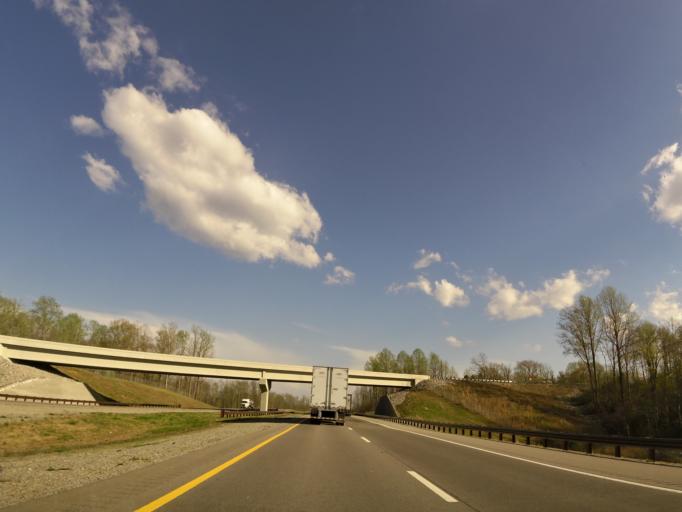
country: US
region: Tennessee
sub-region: Williamson County
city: Fairview
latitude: 35.8476
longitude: -87.0675
